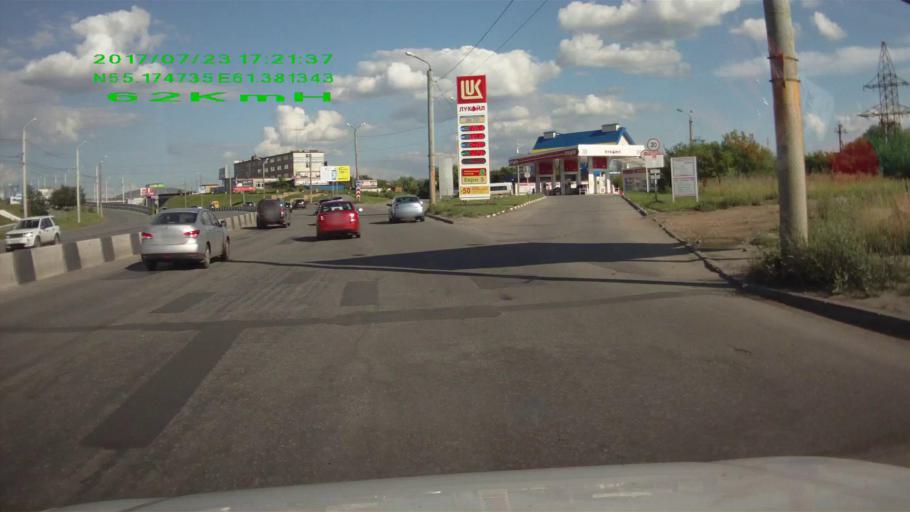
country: RU
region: Chelyabinsk
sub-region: Gorod Chelyabinsk
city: Chelyabinsk
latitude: 55.1745
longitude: 61.3820
